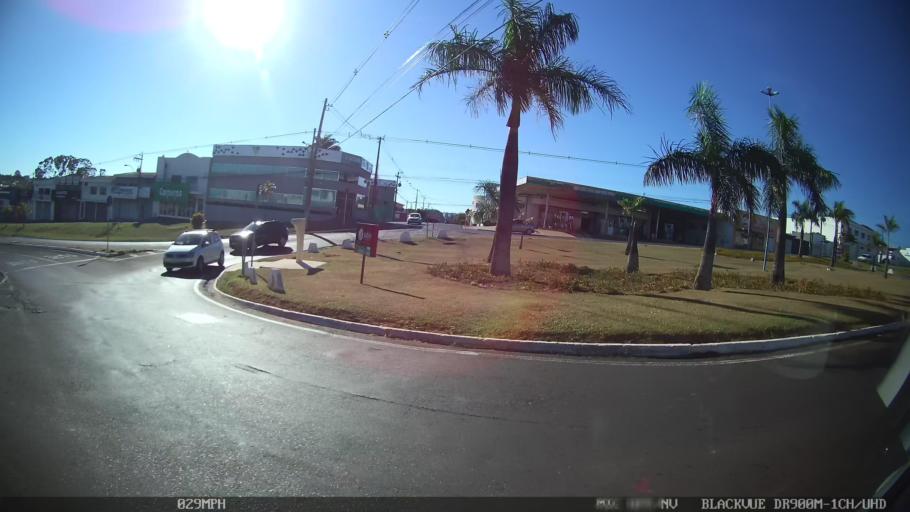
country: BR
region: Sao Paulo
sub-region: Franca
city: Franca
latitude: -20.5573
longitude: -47.3960
